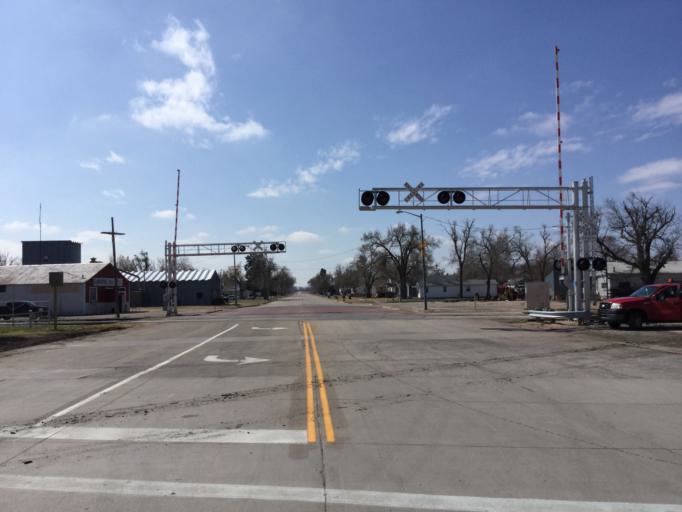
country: US
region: Kansas
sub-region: Barton County
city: Ellinwood
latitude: 38.3537
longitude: -98.5812
